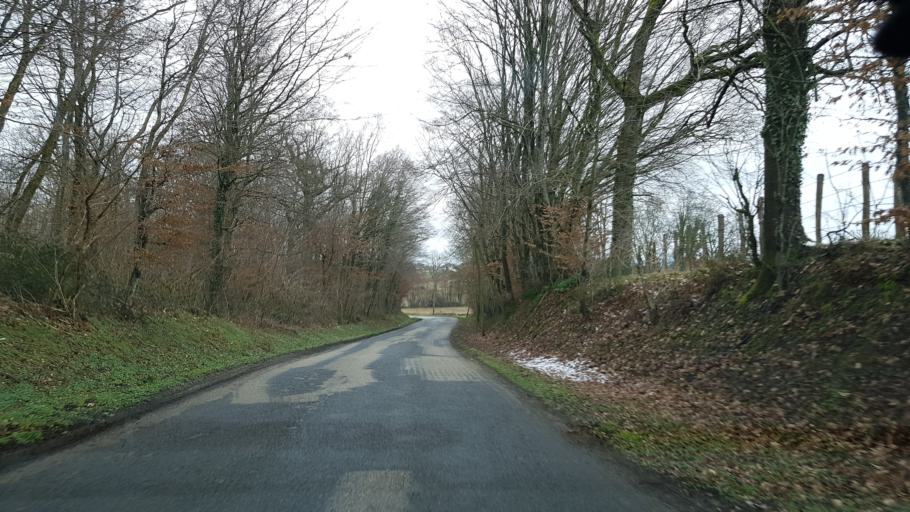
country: FR
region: Rhone-Alpes
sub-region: Departement de l'Ain
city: Saint-Denis-les-Bourg
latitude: 46.1896
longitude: 5.1848
